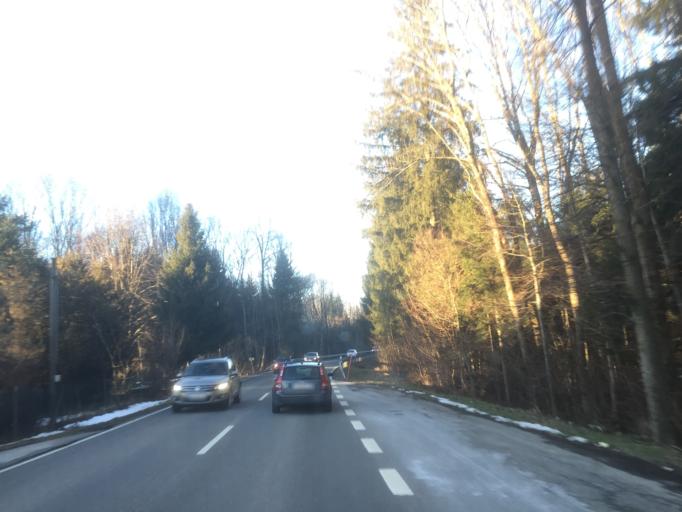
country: DE
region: Bavaria
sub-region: Upper Bavaria
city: Vachendorf
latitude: 47.8430
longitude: 12.6318
